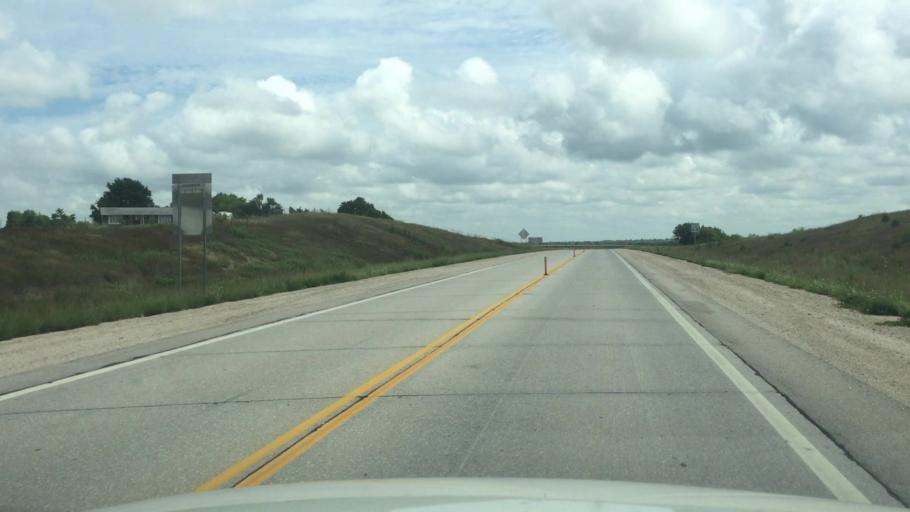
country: US
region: Kansas
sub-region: Allen County
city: Iola
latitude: 37.8872
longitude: -95.3907
